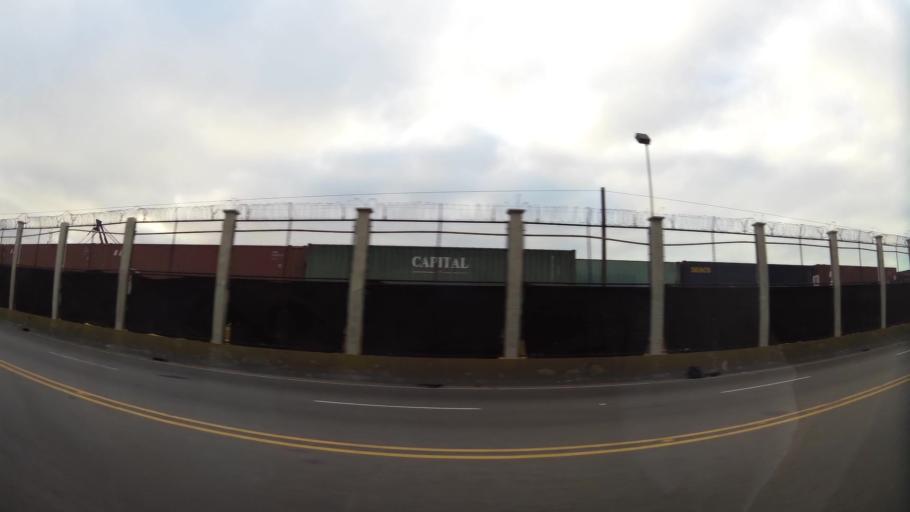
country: DO
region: Nacional
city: Ciudad Nueva
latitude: 18.4707
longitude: -69.8822
